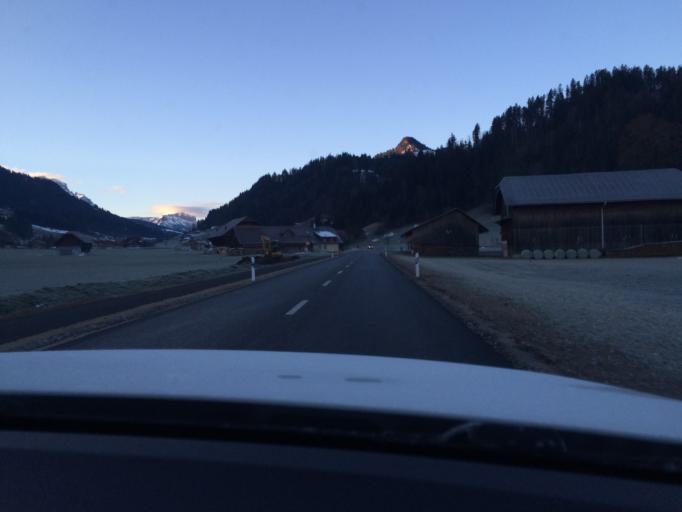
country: CH
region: Lucerne
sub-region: Entlebuch District
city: Escholzmatt
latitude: 46.8644
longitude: 7.9046
